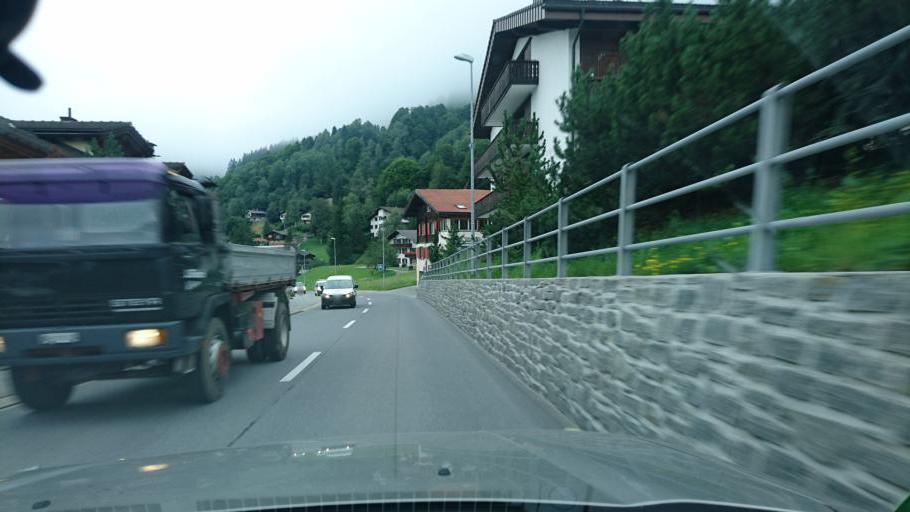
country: CH
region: Grisons
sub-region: Praettigau/Davos District
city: Klosters Serneus
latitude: 46.8787
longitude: 9.8799
